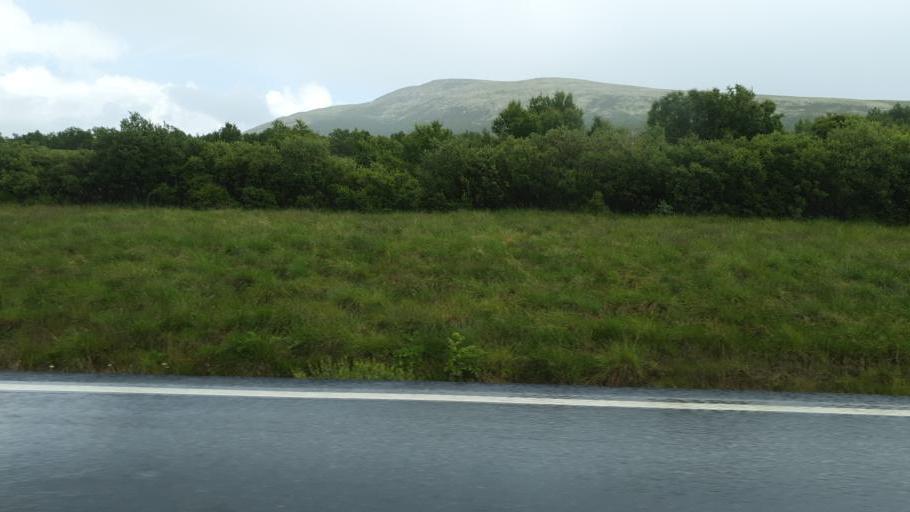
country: NO
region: Sor-Trondelag
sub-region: Oppdal
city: Oppdal
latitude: 62.2501
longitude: 9.5404
